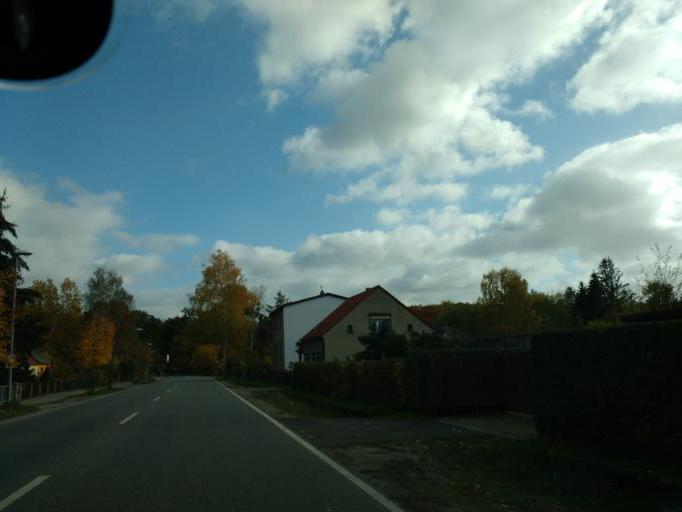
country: DE
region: Brandenburg
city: Petershagen
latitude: 52.5592
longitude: 13.7736
